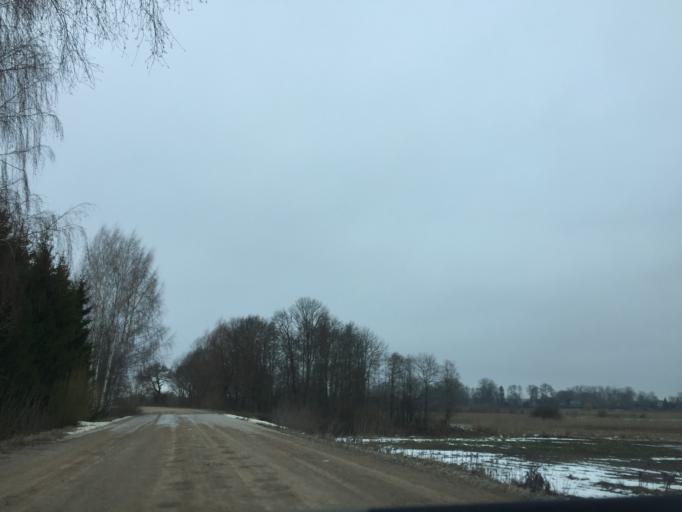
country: LV
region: Ozolnieku
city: Ozolnieki
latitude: 56.6341
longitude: 23.8022
